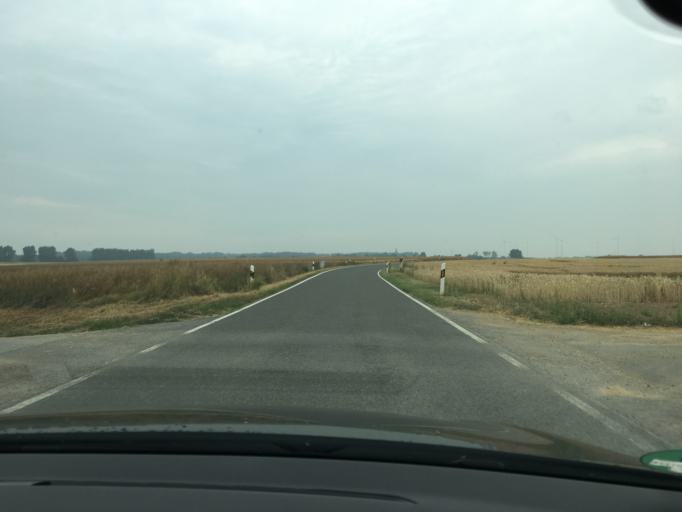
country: DE
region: North Rhine-Westphalia
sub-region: Regierungsbezirk Koln
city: Titz
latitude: 51.0692
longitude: 6.4088
